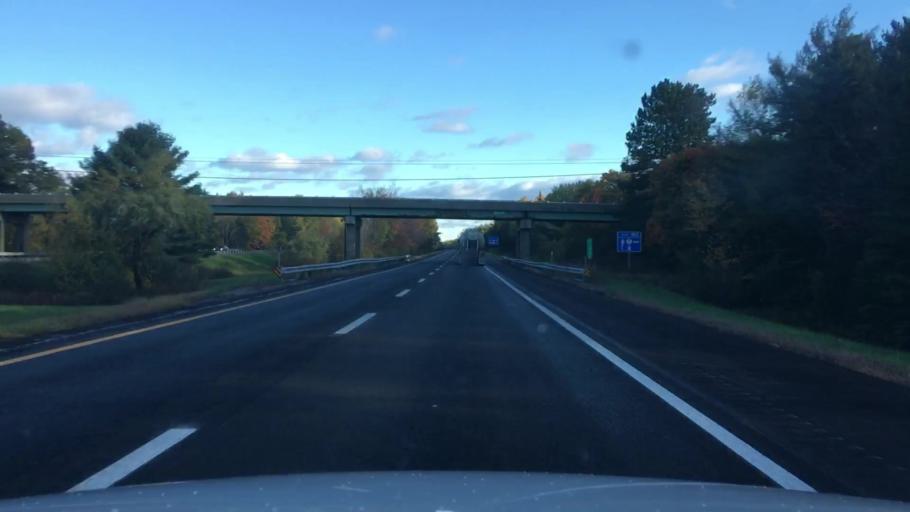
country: US
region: Maine
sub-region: Penobscot County
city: Orono
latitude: 44.8888
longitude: -68.6934
